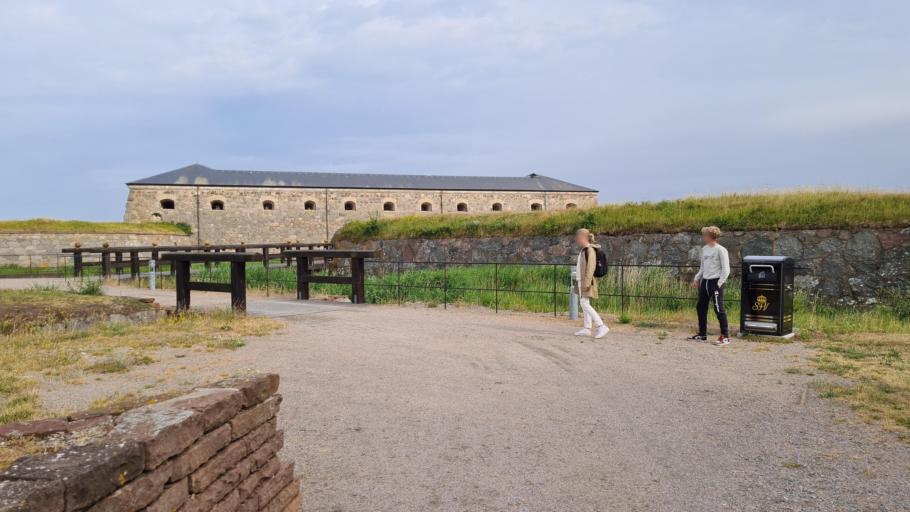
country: SE
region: Blekinge
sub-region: Karlskrona Kommun
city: Karlskrona
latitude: 56.1111
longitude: 15.5626
